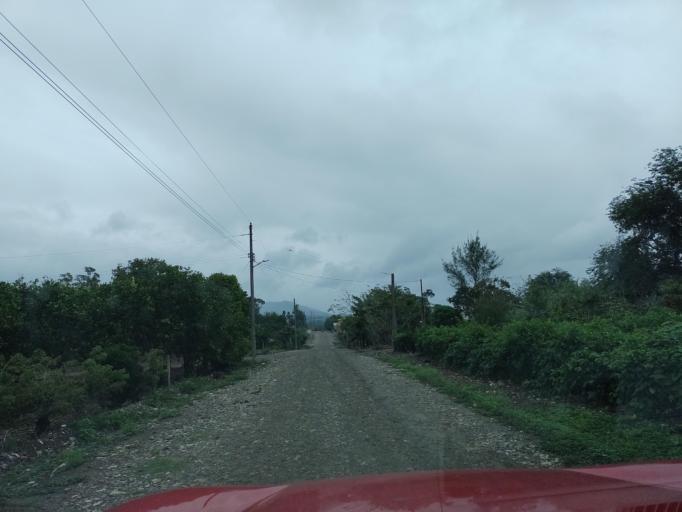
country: MX
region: Veracruz
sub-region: Papantla
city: El Chote
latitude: 20.4133
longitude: -97.3658
